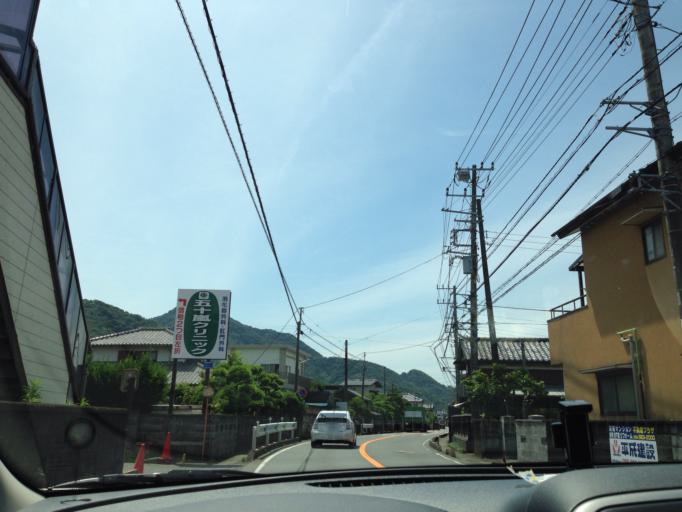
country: JP
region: Shizuoka
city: Numazu
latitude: 35.0723
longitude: 138.8746
